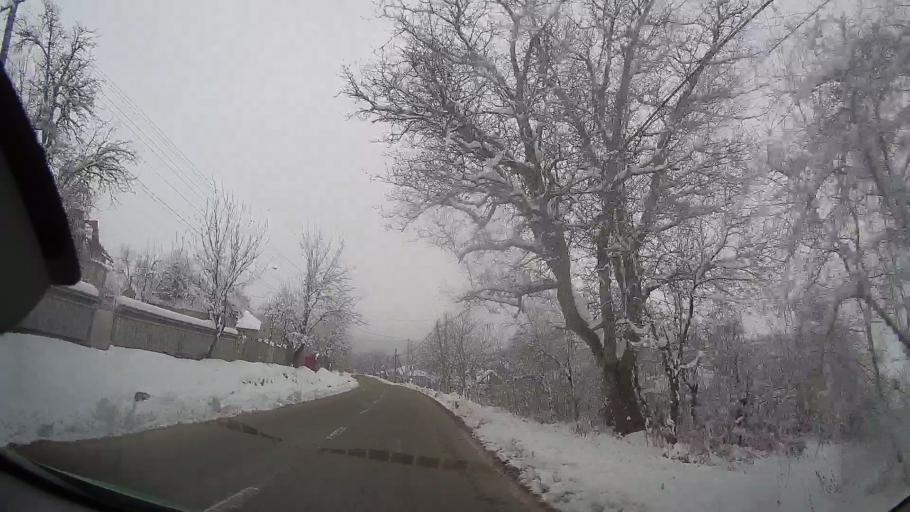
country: RO
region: Neamt
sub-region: Comuna Bozieni
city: Bozieni
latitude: 46.8406
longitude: 27.1478
